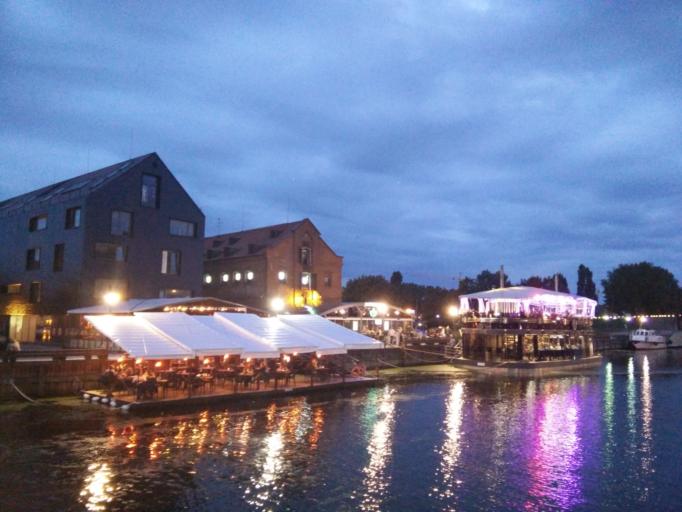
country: LT
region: Klaipedos apskritis
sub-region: Klaipeda
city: Klaipeda
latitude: 55.7096
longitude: 21.1308
